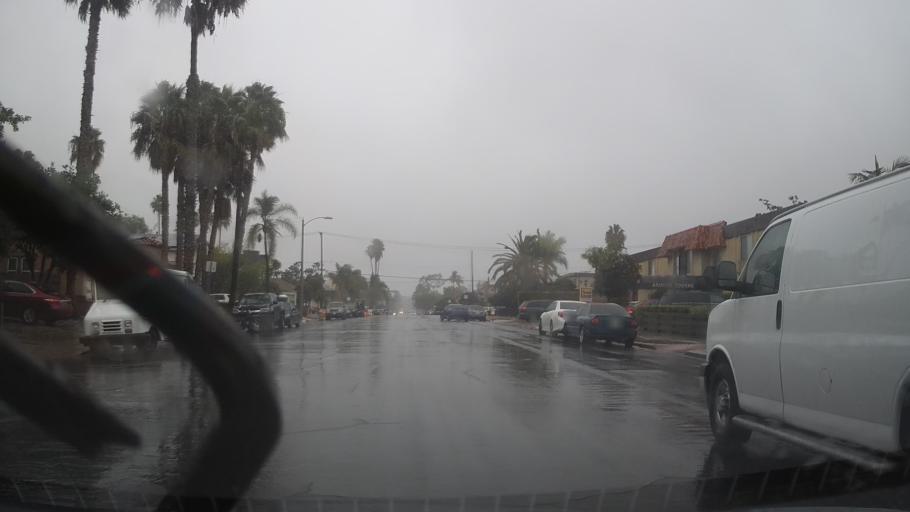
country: US
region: California
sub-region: San Diego County
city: San Diego
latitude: 32.7510
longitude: -117.1376
